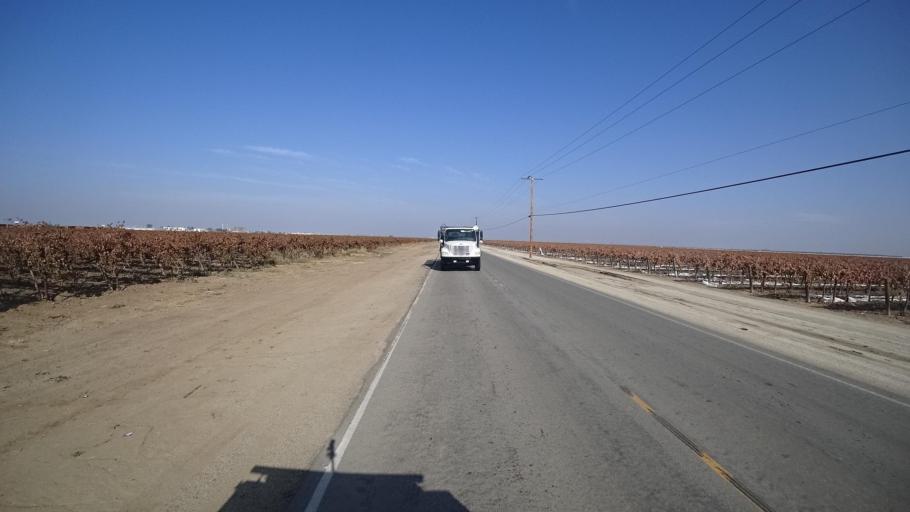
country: US
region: California
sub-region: Kern County
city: McFarland
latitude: 35.7046
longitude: -119.2230
